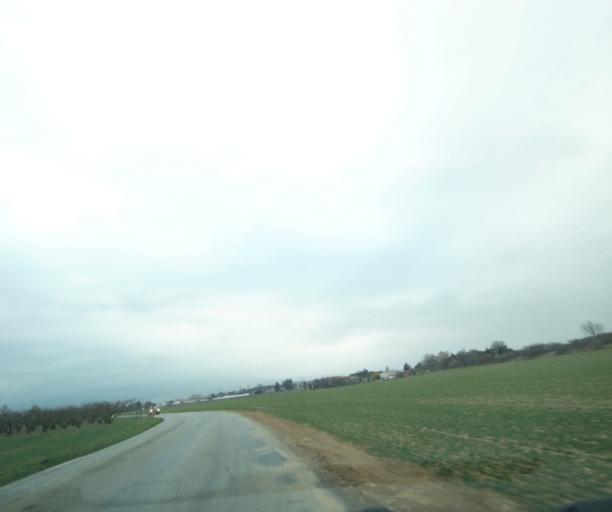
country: FR
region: Rhone-Alpes
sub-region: Departement de la Drome
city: Bourg-les-Valence
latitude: 44.9669
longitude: 4.9235
